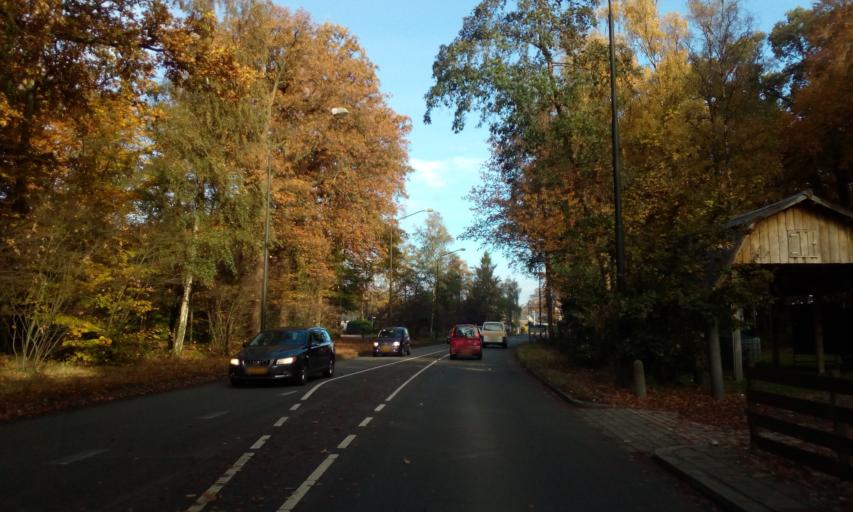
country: NL
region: Gelderland
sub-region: Gemeente Apeldoorn
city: Apeldoorn
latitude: 52.1991
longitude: 5.9466
